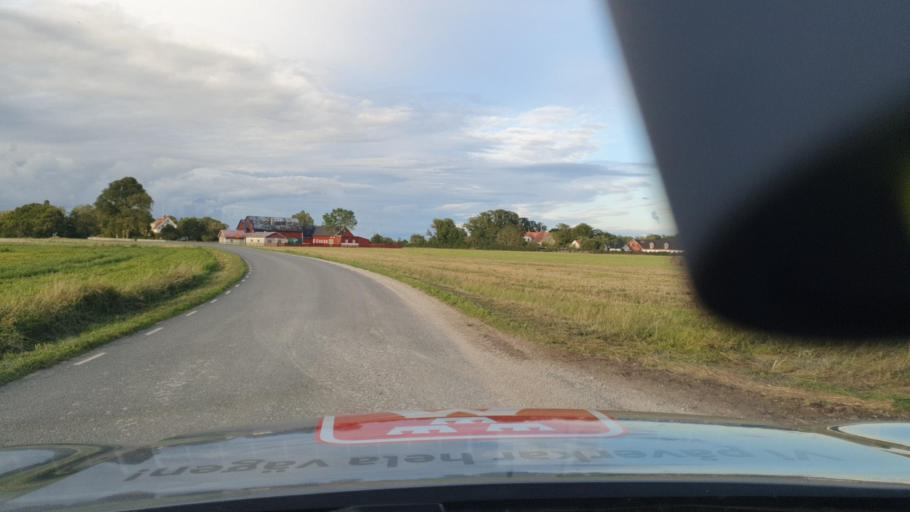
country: SE
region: Gotland
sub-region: Gotland
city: Vibble
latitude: 57.5141
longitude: 18.3232
